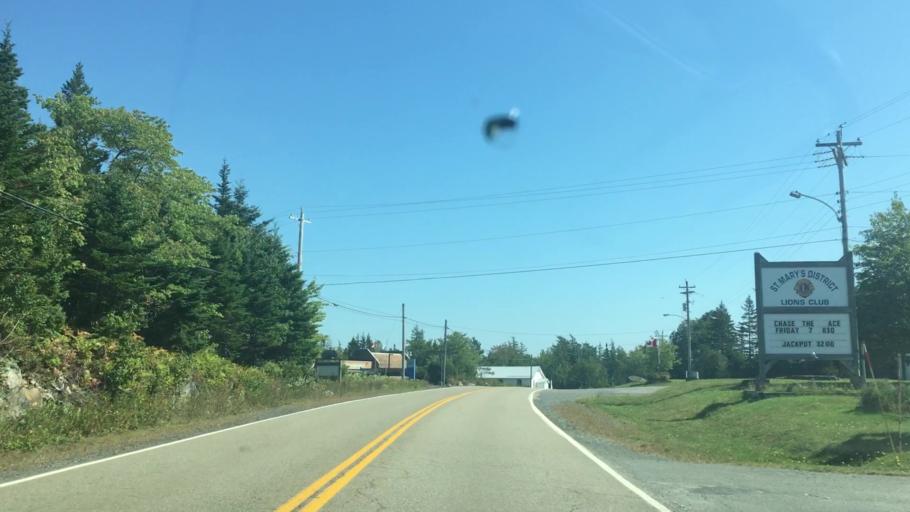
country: CA
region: Nova Scotia
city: Antigonish
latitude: 45.1446
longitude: -61.9901
